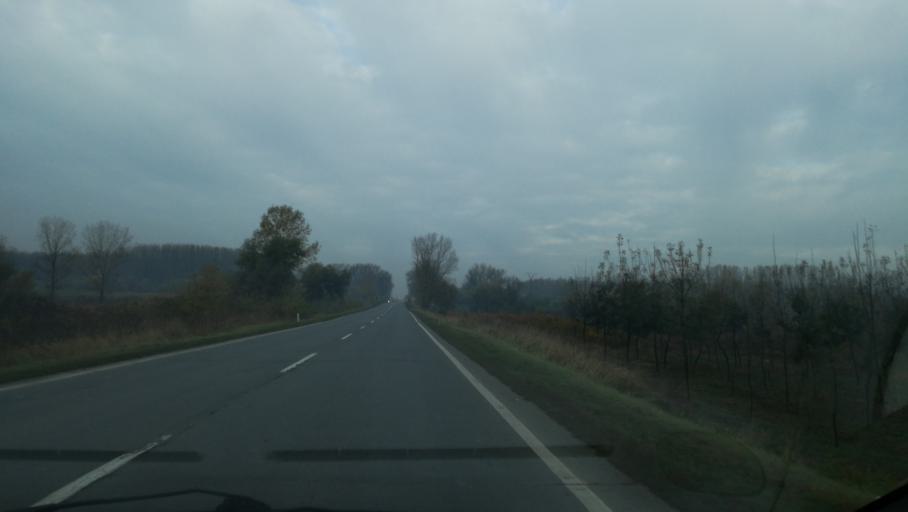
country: RS
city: Taras
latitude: 45.3929
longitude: 20.2230
